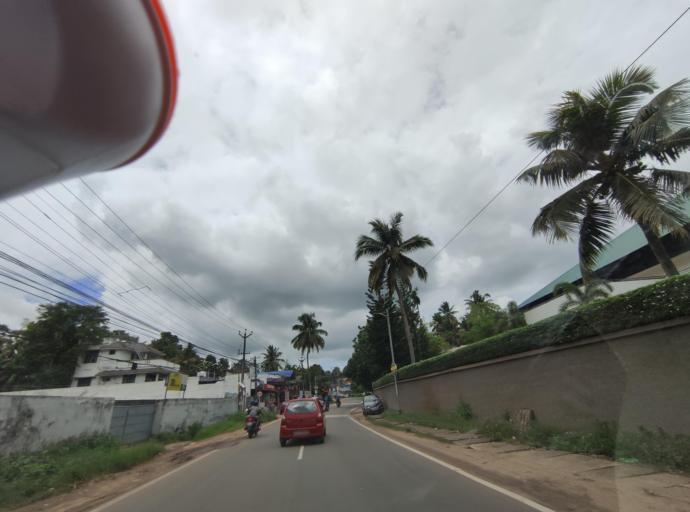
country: IN
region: Kerala
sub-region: Thiruvananthapuram
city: Nedumangad
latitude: 8.5658
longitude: 76.9442
